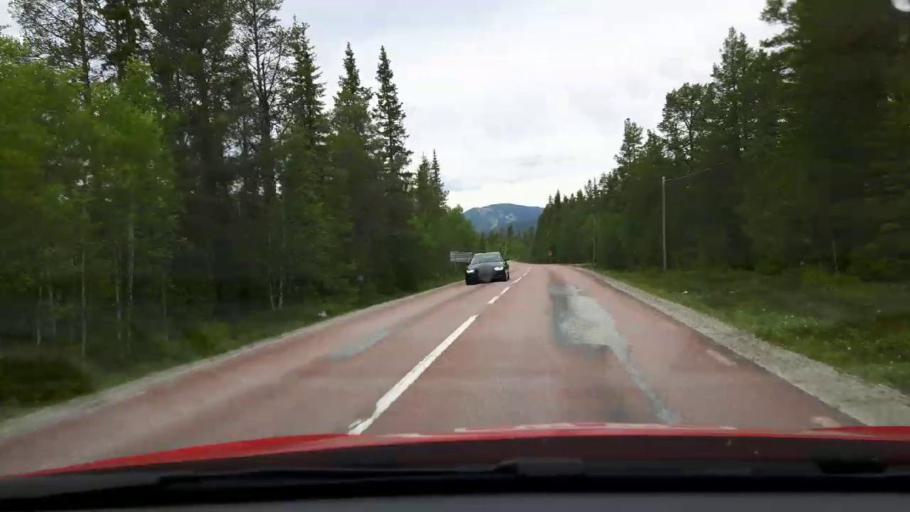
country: NO
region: Hedmark
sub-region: Engerdal
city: Engerdal
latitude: 62.5014
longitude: 12.6261
